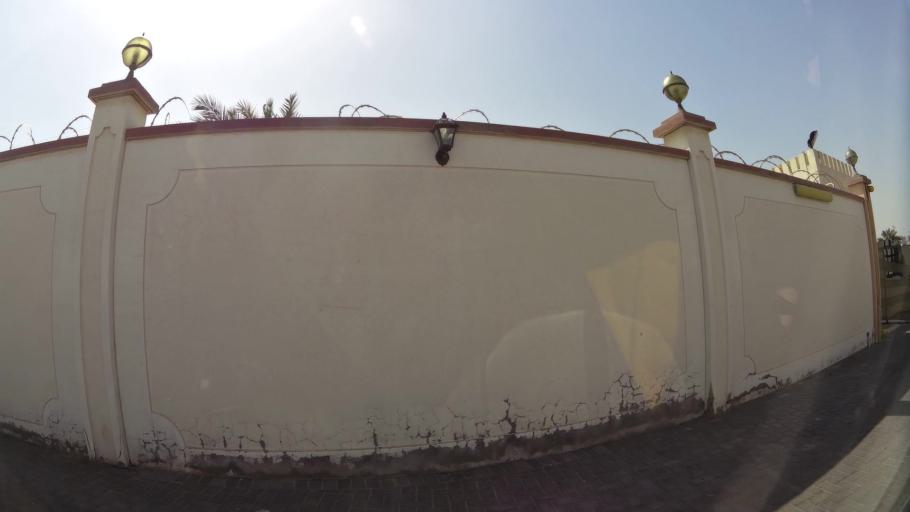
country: BH
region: Northern
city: Madinat `Isa
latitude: 26.1941
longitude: 50.4575
